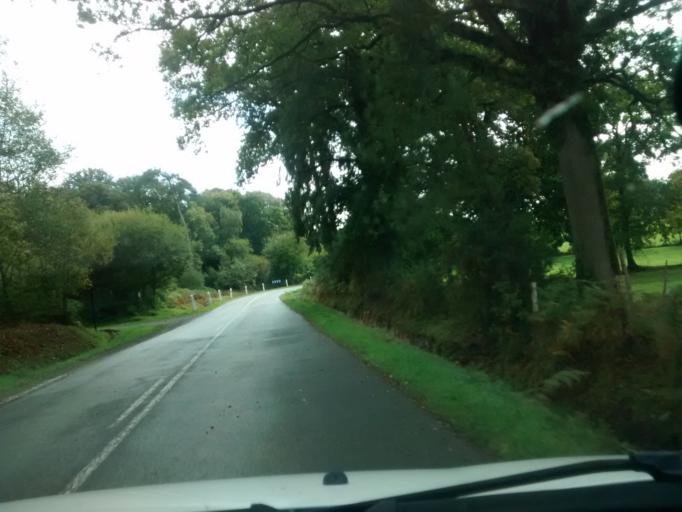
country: FR
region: Brittany
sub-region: Departement d'Ille-et-Vilaine
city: Chateaubourg
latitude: 48.1431
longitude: -1.4012
